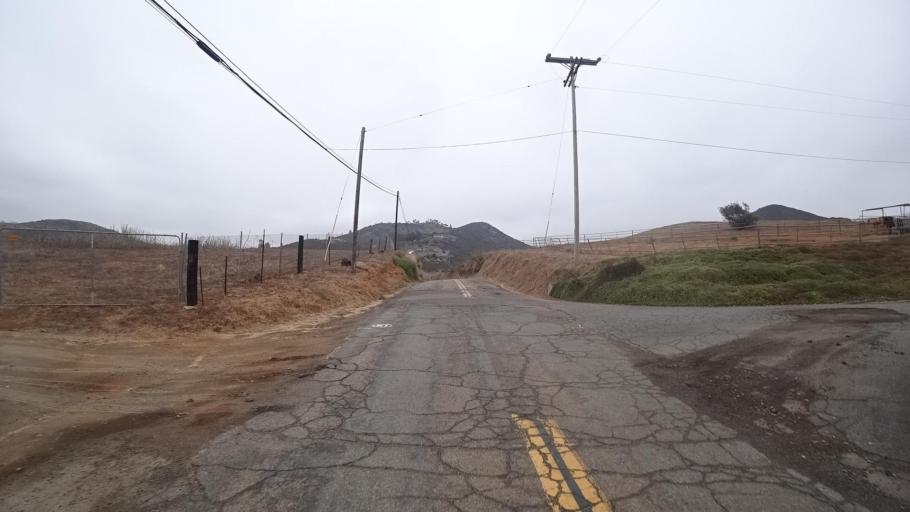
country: US
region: California
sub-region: San Diego County
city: Escondido
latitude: 33.0948
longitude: -117.1326
